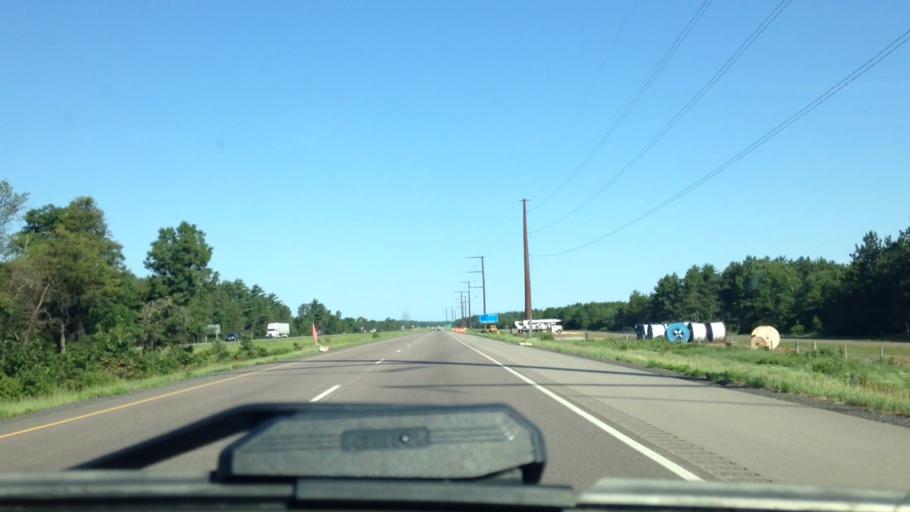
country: US
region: Wisconsin
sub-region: Monroe County
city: Tomah
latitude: 44.1855
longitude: -90.6219
